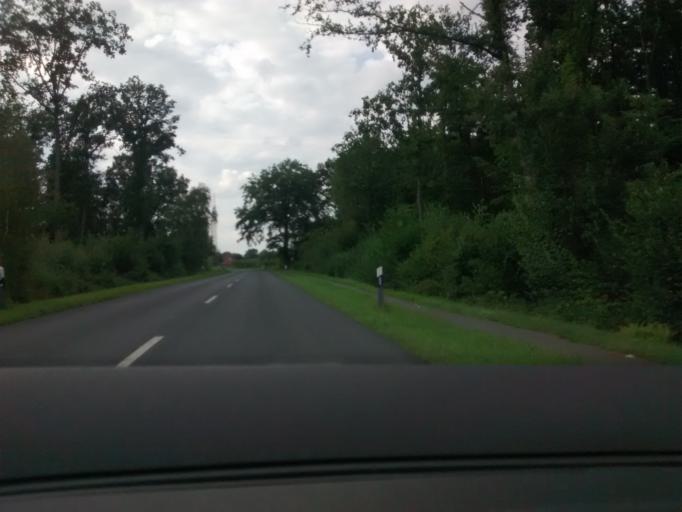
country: DE
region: Lower Saxony
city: Brietlingen
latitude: 53.3250
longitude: 10.4648
